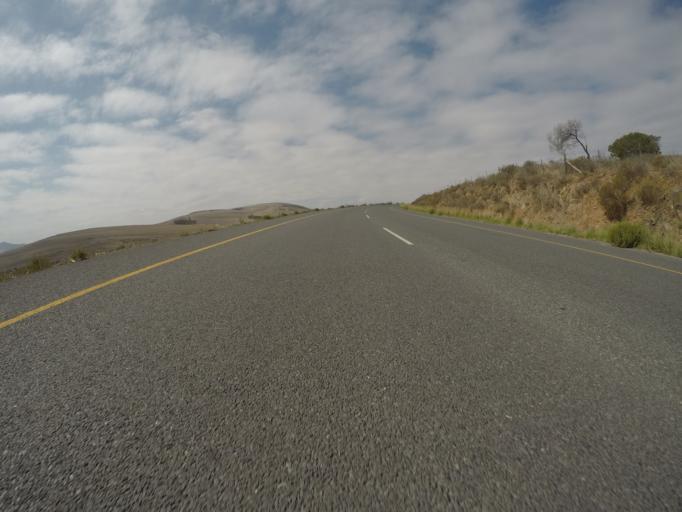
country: ZA
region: Western Cape
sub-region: City of Cape Town
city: Sunset Beach
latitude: -33.7894
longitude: 18.5726
